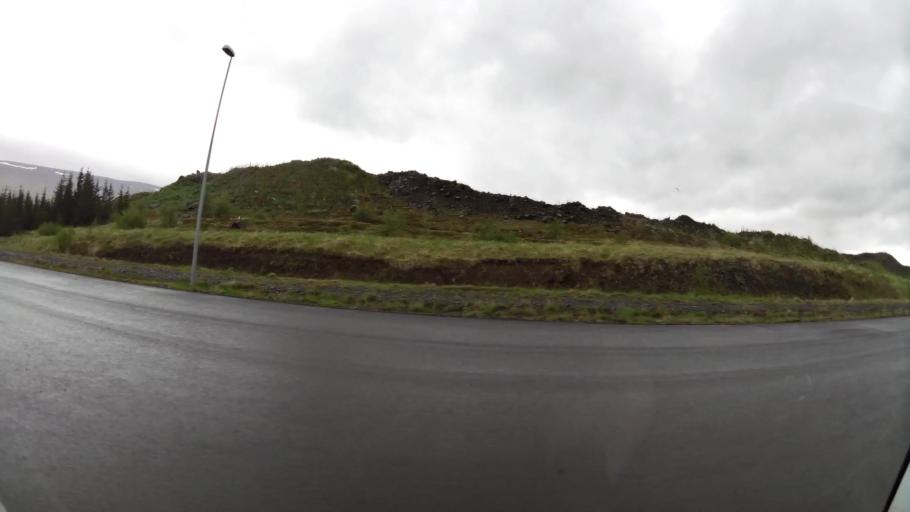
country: IS
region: Northeast
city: Akureyri
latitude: 65.7029
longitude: -18.1287
